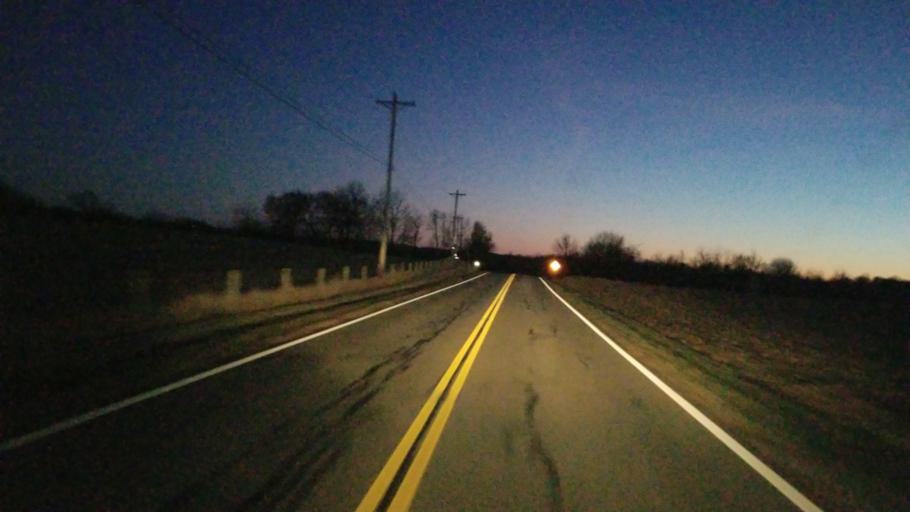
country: US
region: Ohio
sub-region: Highland County
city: Leesburg
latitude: 39.3107
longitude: -83.5236
